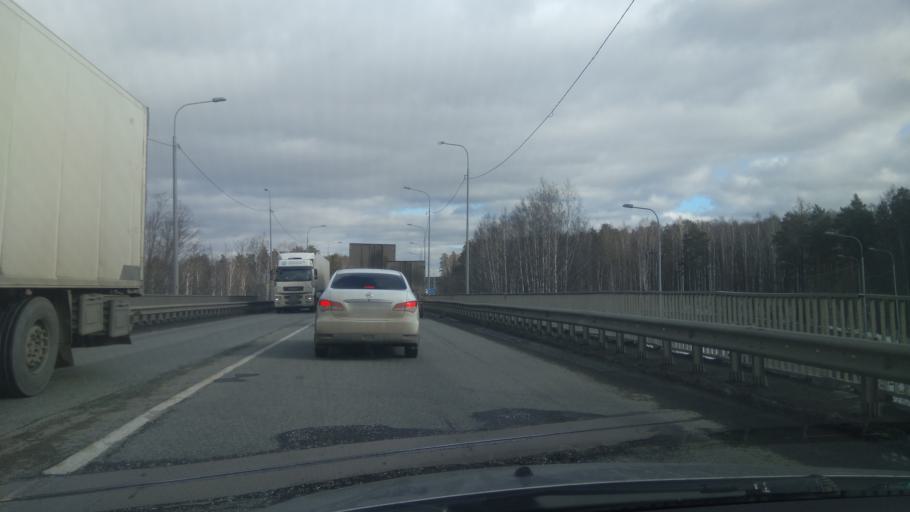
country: RU
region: Sverdlovsk
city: Talitsa
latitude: 56.8499
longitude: 60.0606
